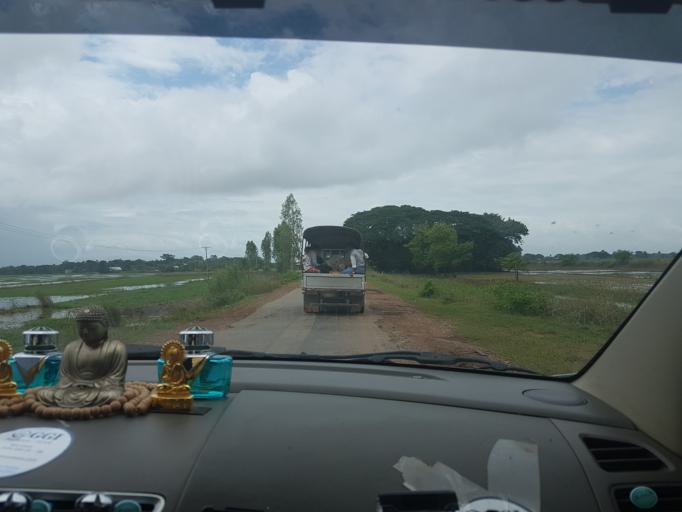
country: MM
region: Bago
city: Nyaunglebin
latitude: 17.9177
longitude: 96.8277
